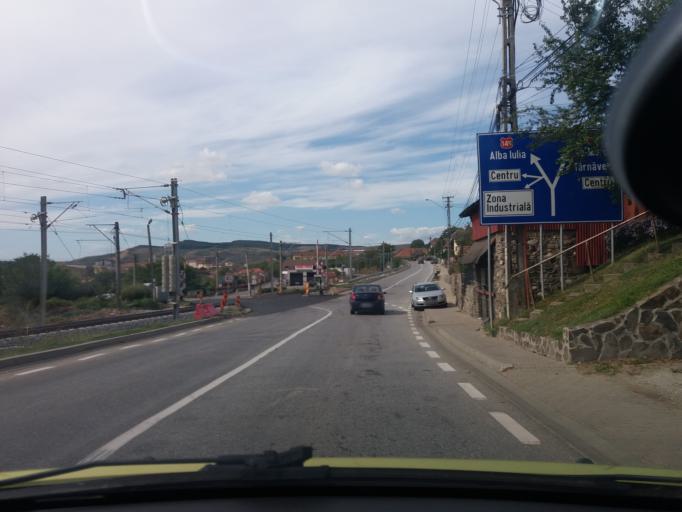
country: RO
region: Alba
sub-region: Municipiul Blaj
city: Veza
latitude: 46.1746
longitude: 23.9372
